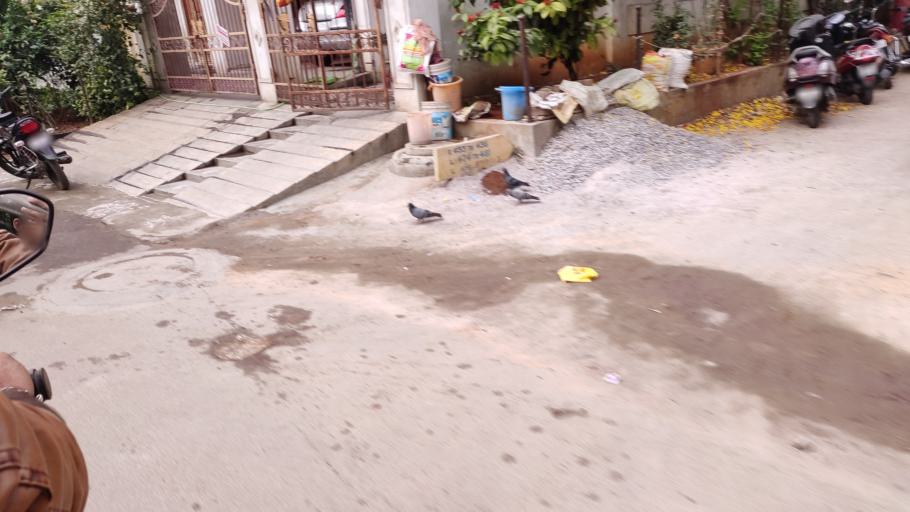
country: IN
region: Telangana
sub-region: Rangareddi
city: Kukatpalli
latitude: 17.4926
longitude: 78.3881
